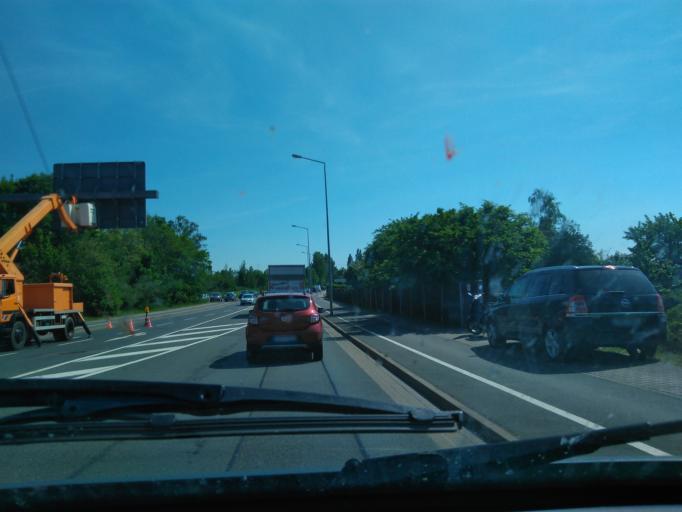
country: DE
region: Saxony
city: Taucha
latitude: 51.3588
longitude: 12.4441
